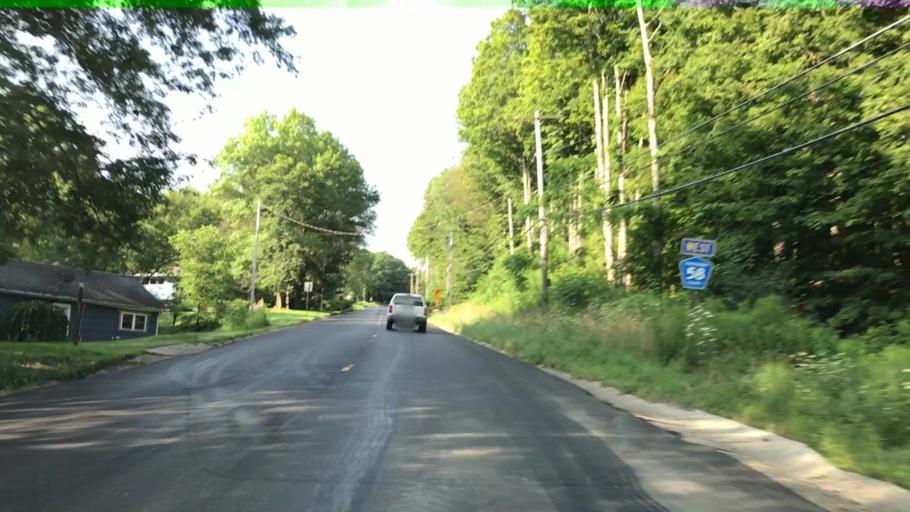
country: US
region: New York
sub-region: Chautauqua County
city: Fredonia
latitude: 42.3351
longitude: -79.3235
